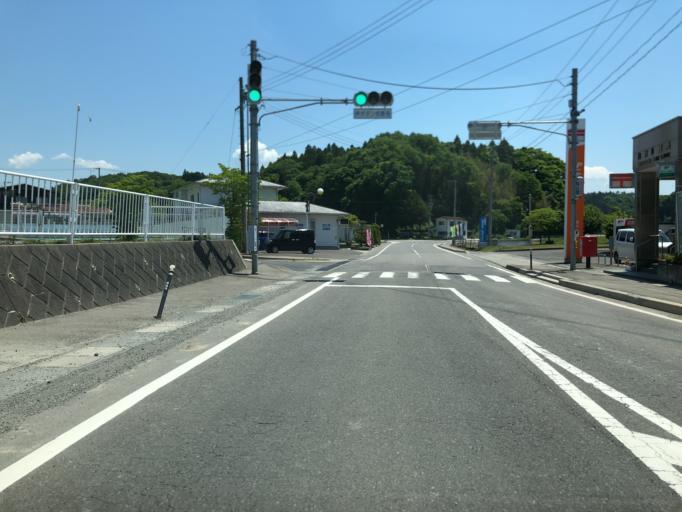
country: JP
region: Fukushima
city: Miharu
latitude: 37.5022
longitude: 140.4741
